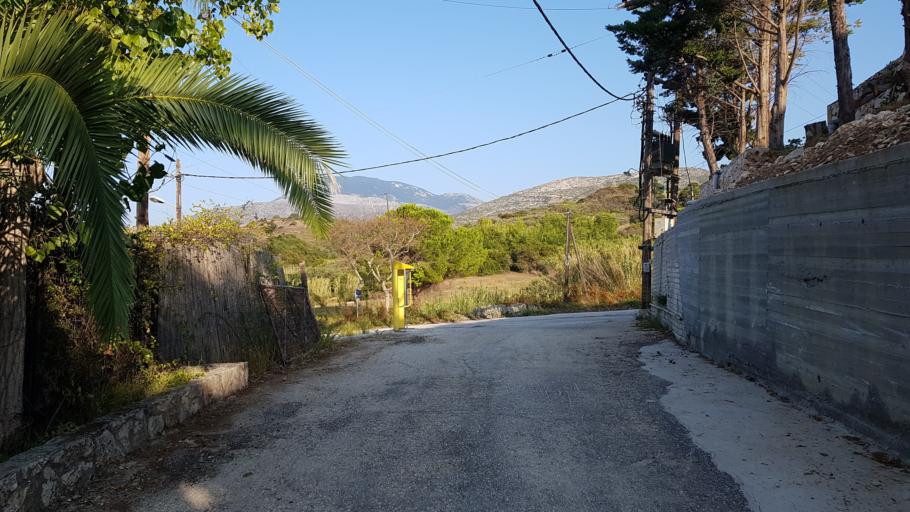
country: GR
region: Ionian Islands
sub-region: Nomos Kefallinias
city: Poros
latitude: 38.0656
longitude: 20.7789
